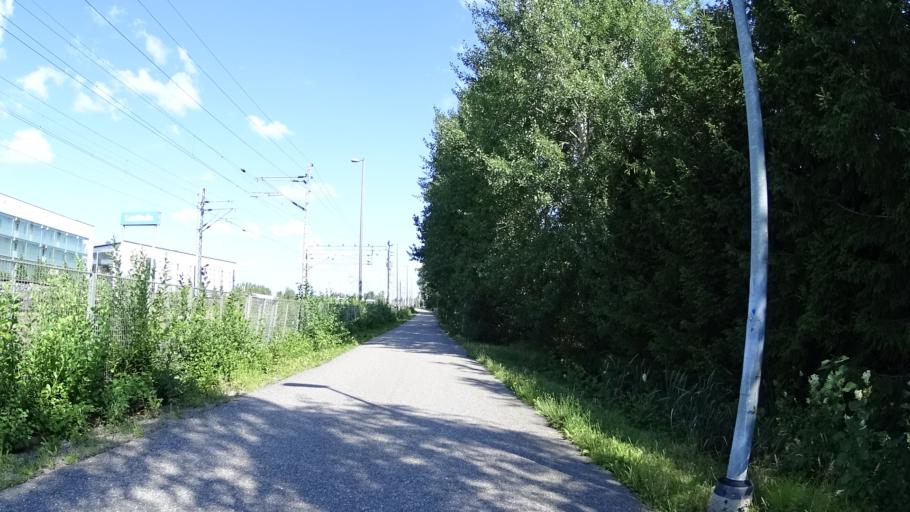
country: FI
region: Uusimaa
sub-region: Helsinki
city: Jaervenpaeae
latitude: 60.4609
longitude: 25.1007
